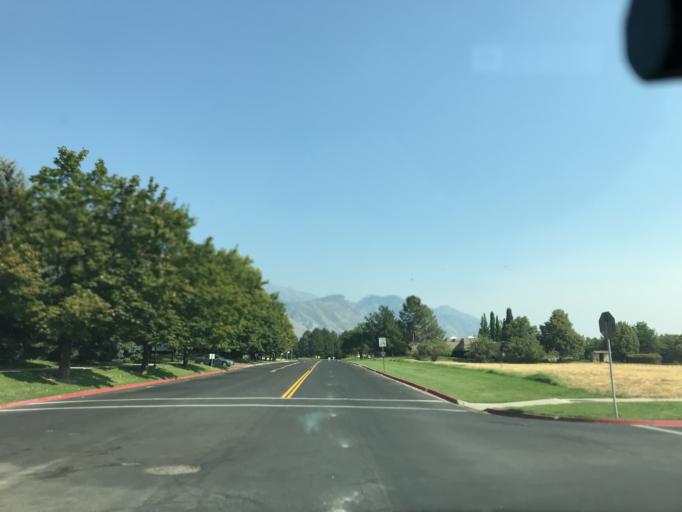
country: US
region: Utah
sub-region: Utah County
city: Orem
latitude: 40.3230
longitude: -111.6804
